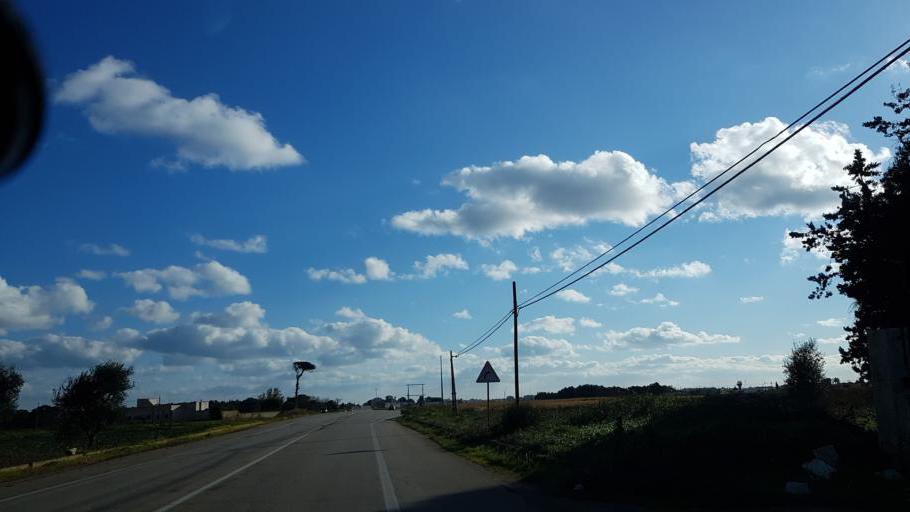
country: IT
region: Apulia
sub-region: Provincia di Brindisi
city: Brindisi
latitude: 40.6455
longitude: 17.9057
